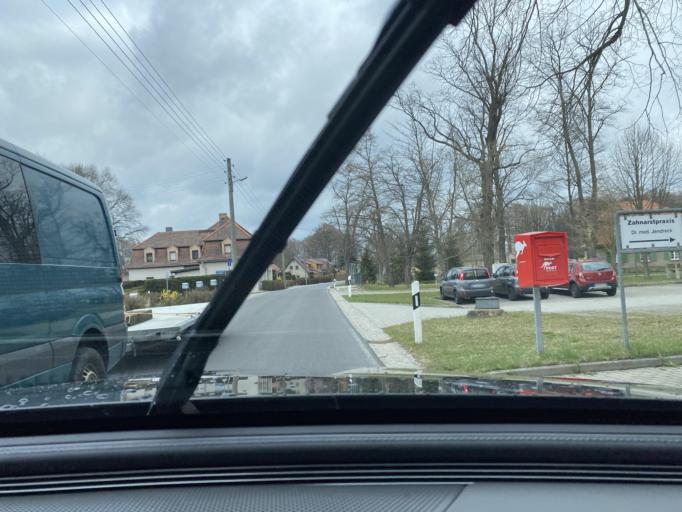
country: DE
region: Saxony
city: Grossdubrau
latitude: 51.3009
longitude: 14.4557
